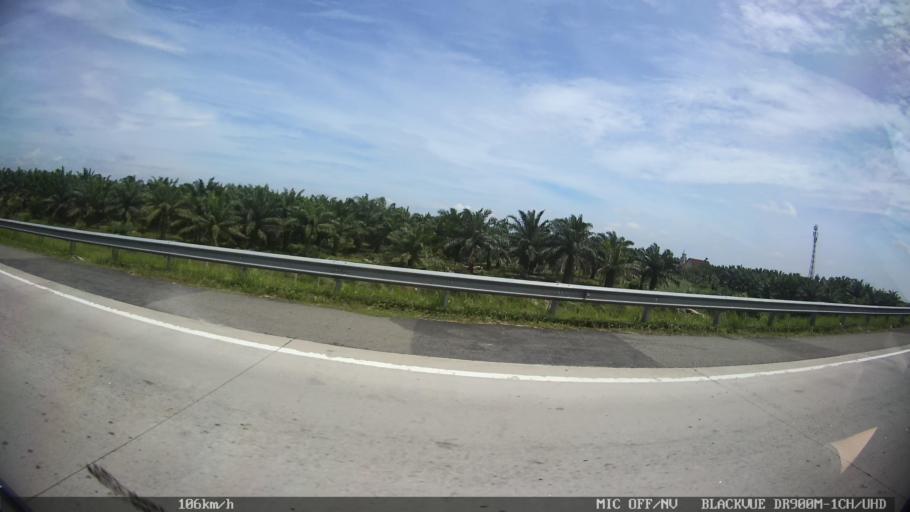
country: ID
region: North Sumatra
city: Perbaungan
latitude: 3.5317
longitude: 98.8848
